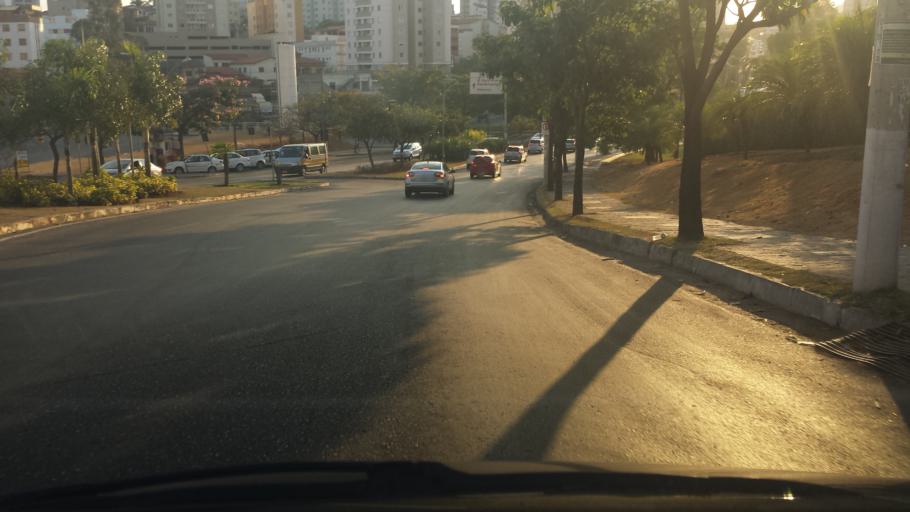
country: BR
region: Minas Gerais
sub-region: Belo Horizonte
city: Belo Horizonte
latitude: -19.8754
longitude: -43.9941
